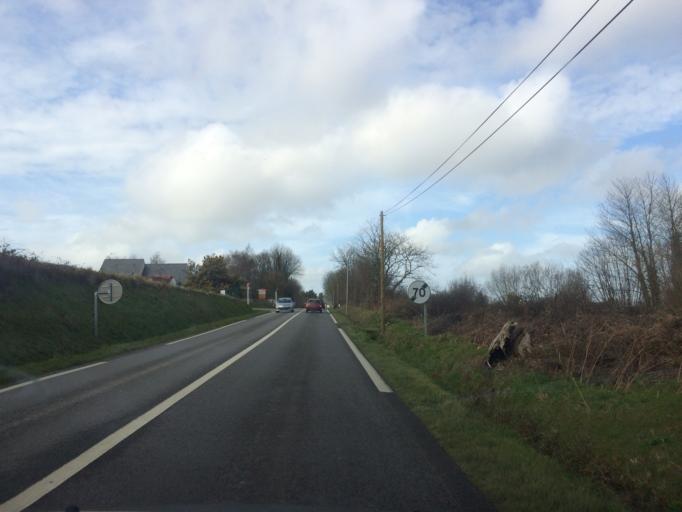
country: FR
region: Brittany
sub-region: Departement du Morbihan
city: Saint-Dolay
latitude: 47.5437
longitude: -2.1430
